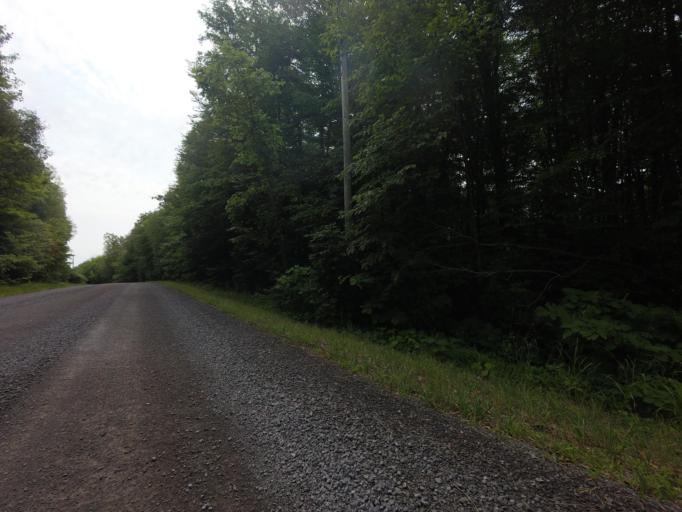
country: CA
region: Ontario
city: Arnprior
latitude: 45.3995
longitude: -76.2110
